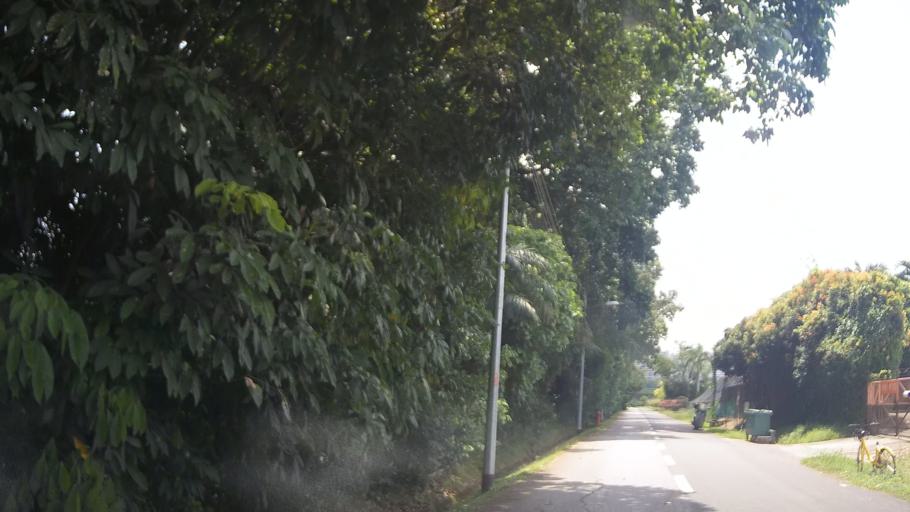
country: MY
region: Johor
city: Kampung Pasir Gudang Baru
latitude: 1.3998
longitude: 103.8654
